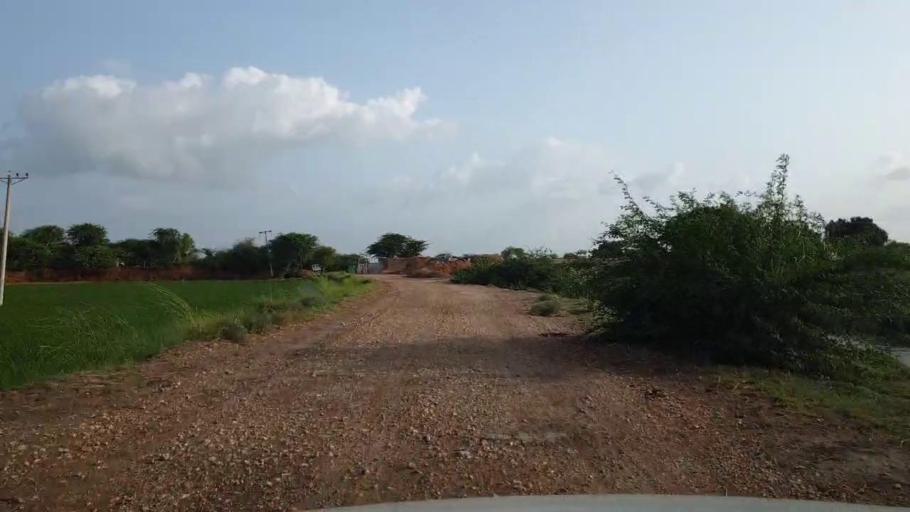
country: PK
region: Sindh
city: Kario
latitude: 24.8215
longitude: 68.6467
